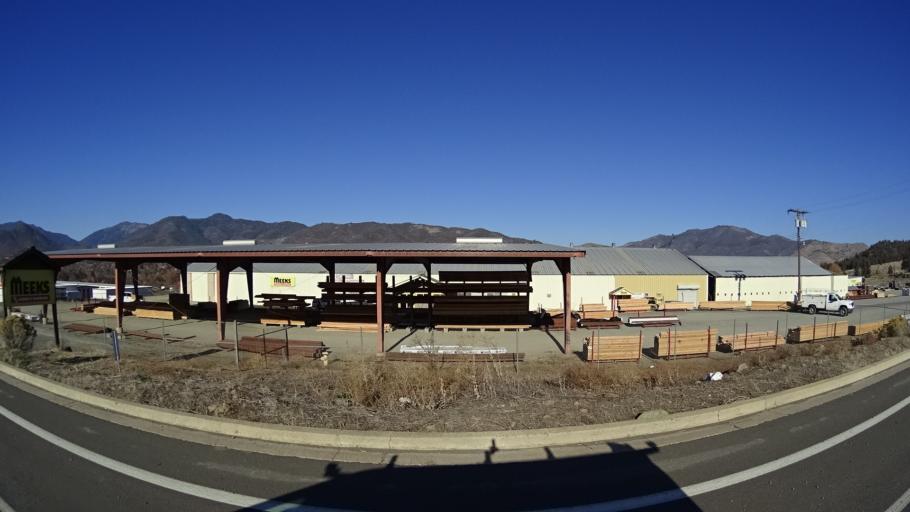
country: US
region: California
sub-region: Siskiyou County
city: Yreka
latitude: 41.7362
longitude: -122.6222
